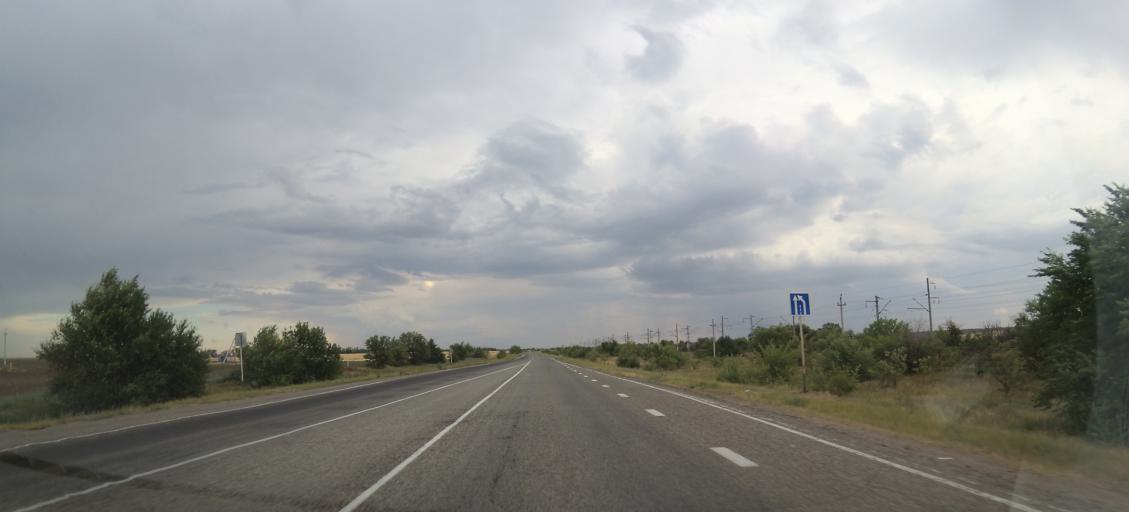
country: RU
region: Rostov
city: Dubovskoye
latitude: 47.4387
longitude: 42.8001
